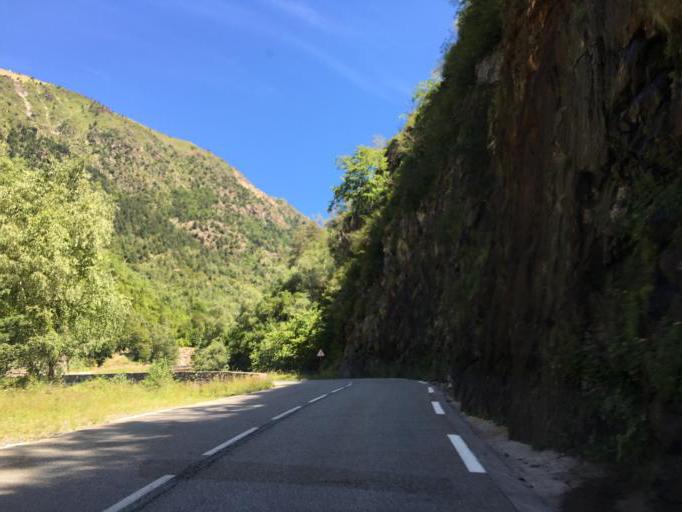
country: IT
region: Piedmont
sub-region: Provincia di Cuneo
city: Sambuco
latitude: 44.1980
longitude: 7.0691
